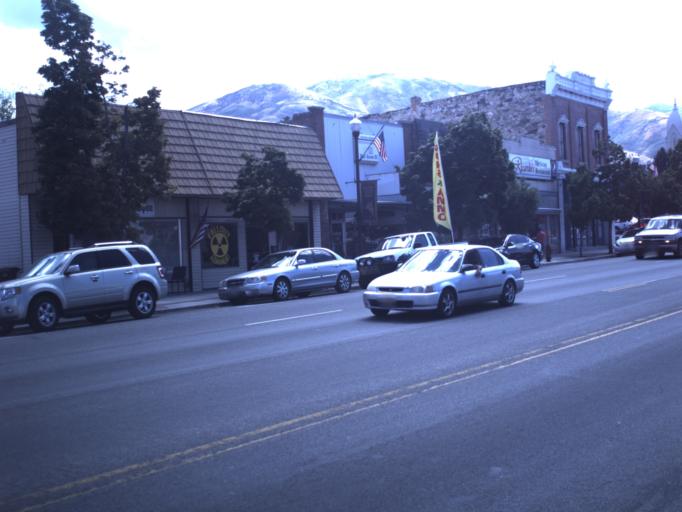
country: US
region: Utah
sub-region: Box Elder County
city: Brigham City
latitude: 41.5077
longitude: -112.0159
